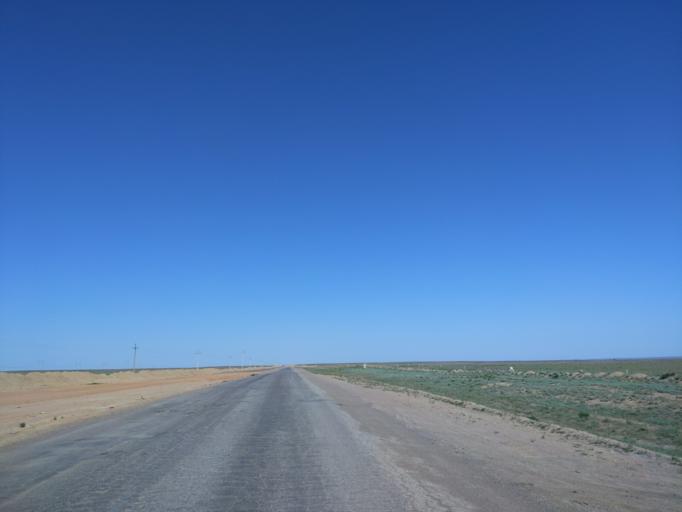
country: KZ
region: Almaty Oblysy
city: Bakanas
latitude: 44.1512
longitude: 75.8619
